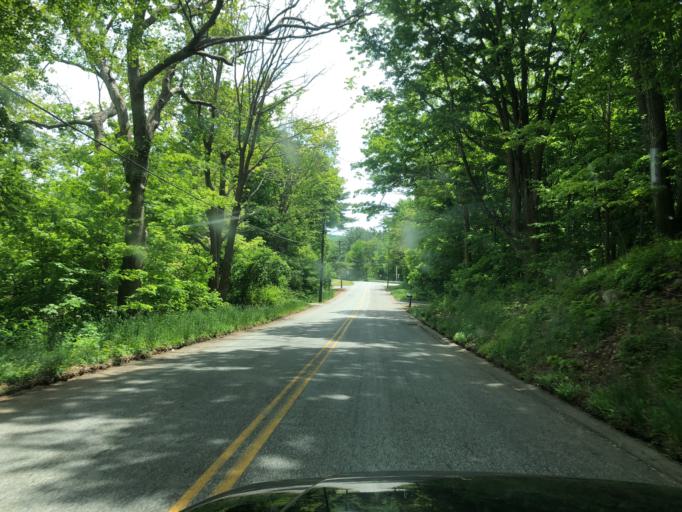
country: US
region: Connecticut
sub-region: Windham County
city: North Grosvenor Dale
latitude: 41.9764
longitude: -71.8874
